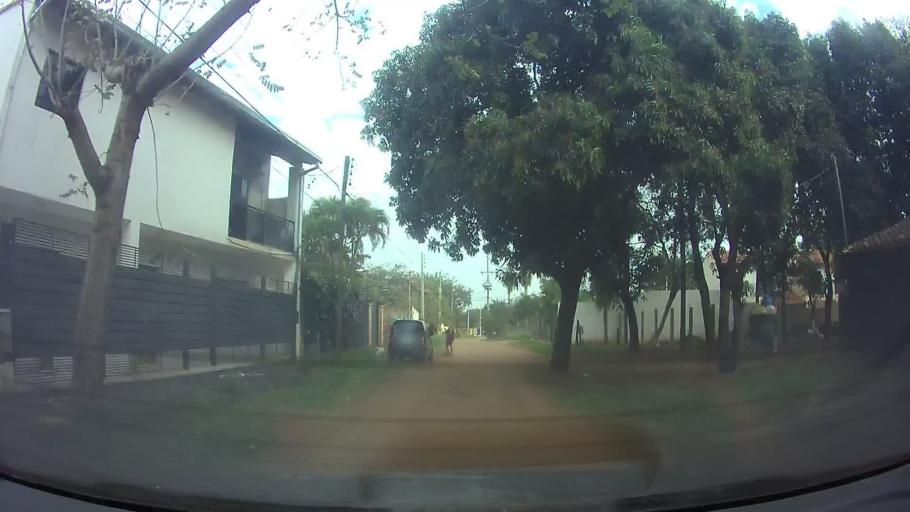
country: PY
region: Central
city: Limpio
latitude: -25.2513
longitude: -57.5071
